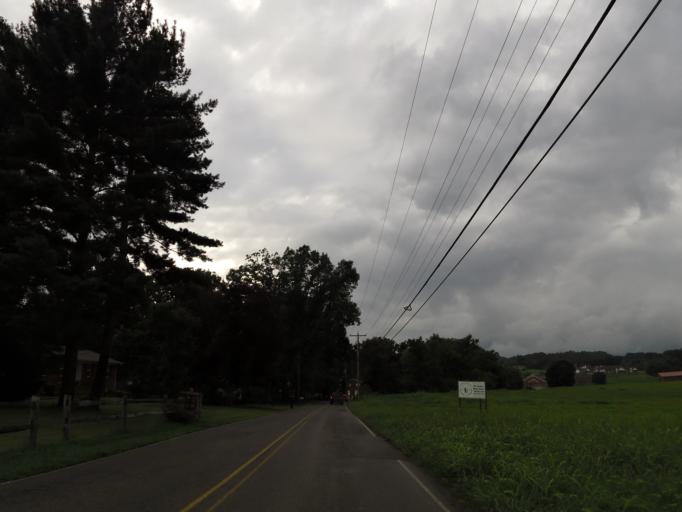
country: US
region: Tennessee
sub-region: Blount County
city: Eagleton Village
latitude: 35.7899
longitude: -83.9050
